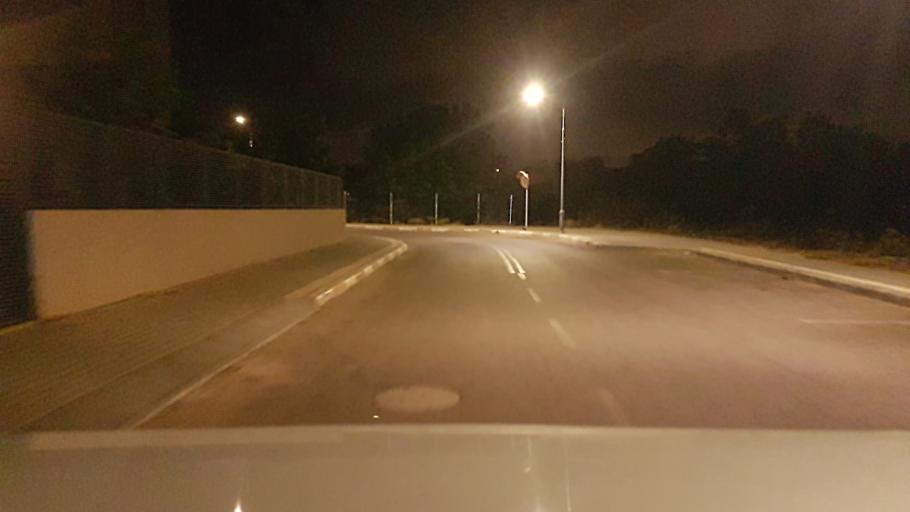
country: IL
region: Central District
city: Nehalim
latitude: 32.0742
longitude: 34.9172
